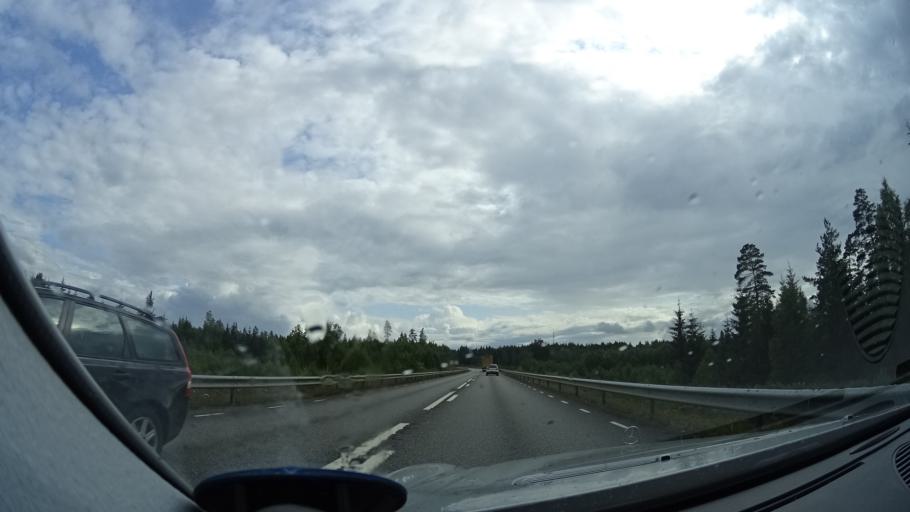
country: SE
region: Blekinge
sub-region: Karlshamns Kommun
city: Svangsta
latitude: 56.3403
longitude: 14.8894
